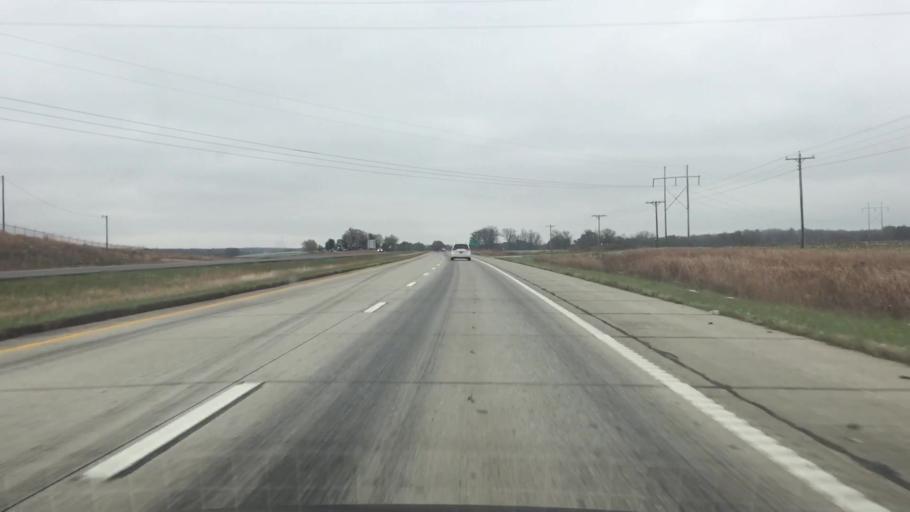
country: US
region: Missouri
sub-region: Saint Clair County
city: Osceola
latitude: 38.0325
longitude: -93.6774
